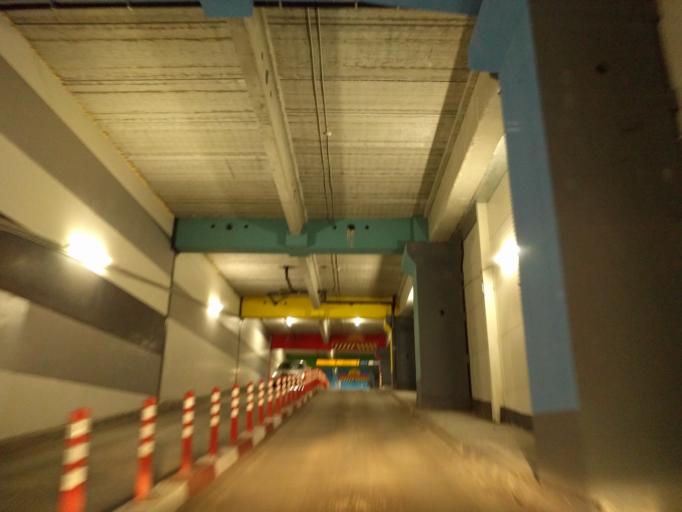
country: RO
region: Ilfov
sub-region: Comuna Fundeni-Dobroesti
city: Fundeni
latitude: 44.4406
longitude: 26.1520
